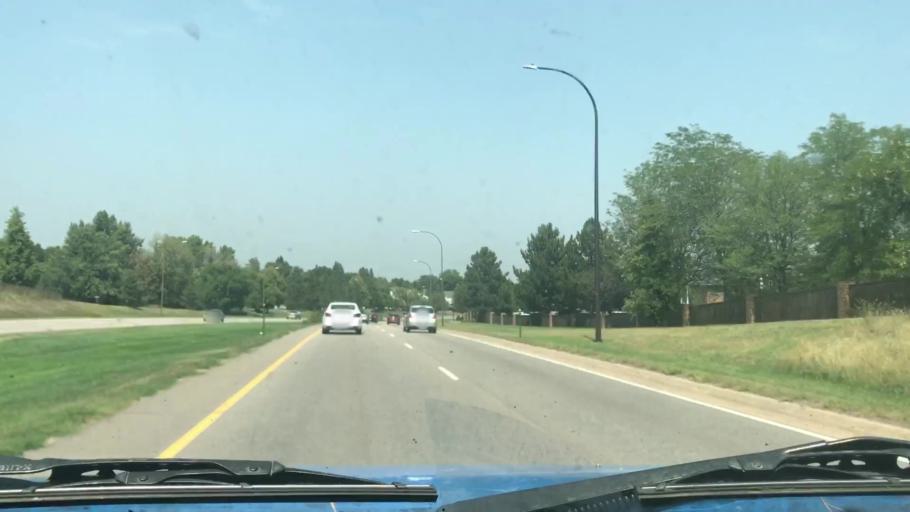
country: US
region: Colorado
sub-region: Jefferson County
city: Lakewood
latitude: 39.6846
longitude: -105.1201
